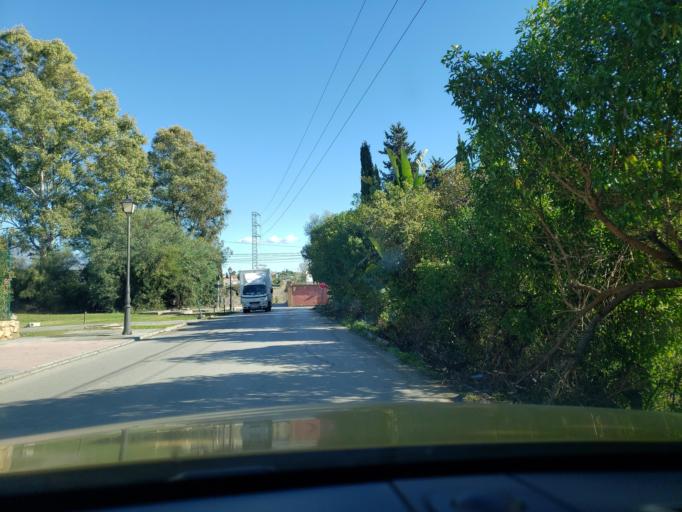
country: ES
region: Andalusia
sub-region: Provincia de Malaga
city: Benahavis
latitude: 36.4852
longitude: -5.0163
